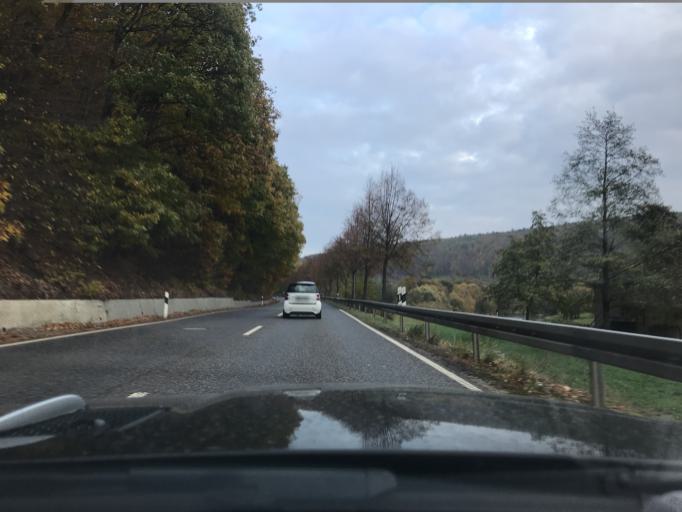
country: DE
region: Lower Saxony
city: Hannoversch Munden
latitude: 51.4039
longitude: 9.6312
